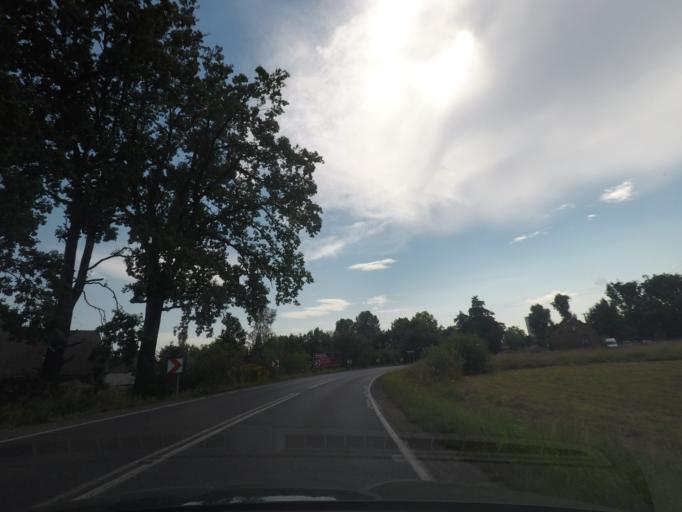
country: PL
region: Lesser Poland Voivodeship
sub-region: Powiat oswiecimski
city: Przecieszyn
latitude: 49.9926
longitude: 19.1692
